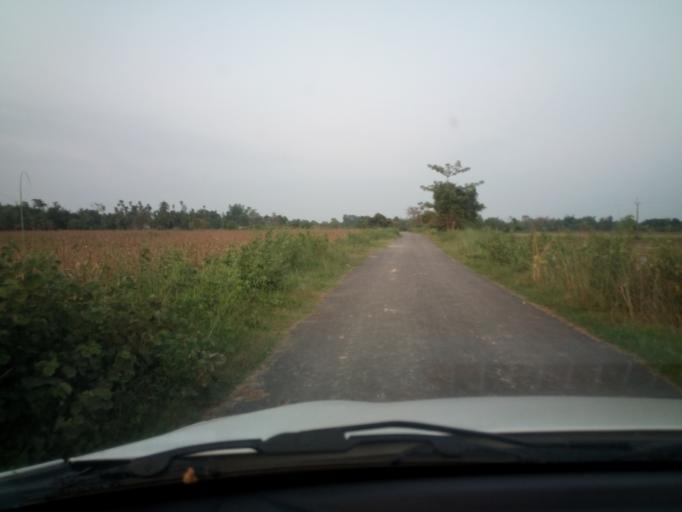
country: IN
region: Assam
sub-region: Udalguri
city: Udalguri
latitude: 26.6843
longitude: 92.1140
